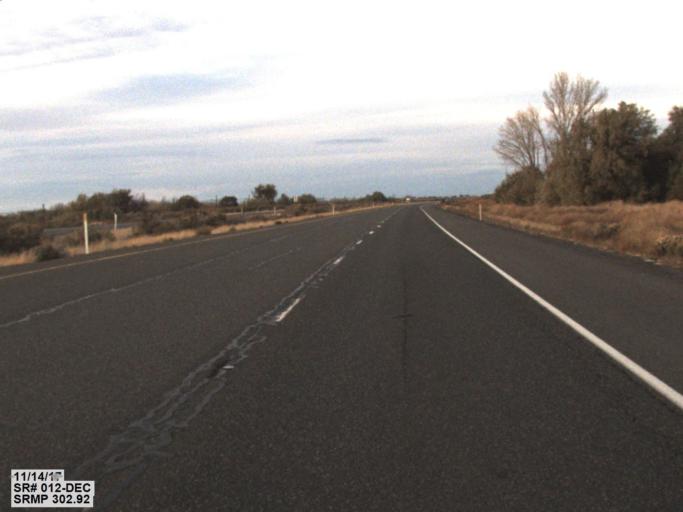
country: US
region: Washington
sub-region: Benton County
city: Finley
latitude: 46.1207
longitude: -118.9277
